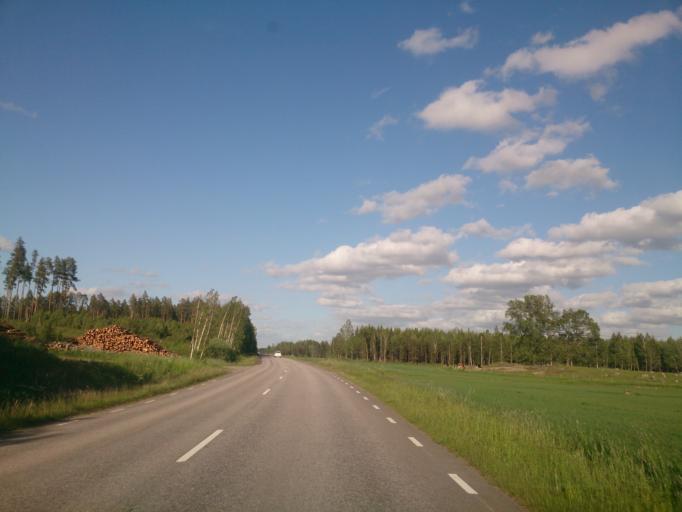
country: SE
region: OEstergoetland
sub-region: Linkopings Kommun
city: Linghem
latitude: 58.4027
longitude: 15.8145
